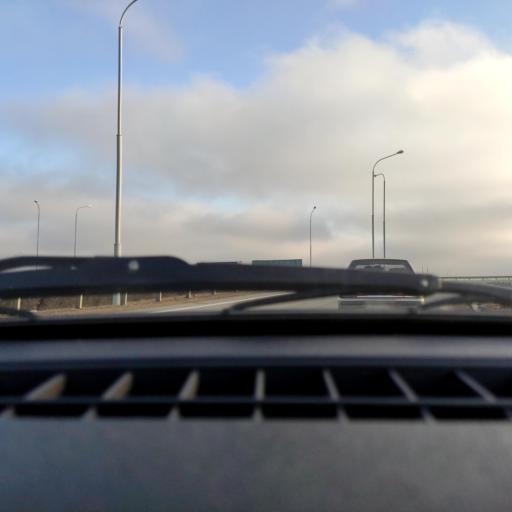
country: RU
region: Bashkortostan
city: Chishmy
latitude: 54.6699
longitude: 55.4011
